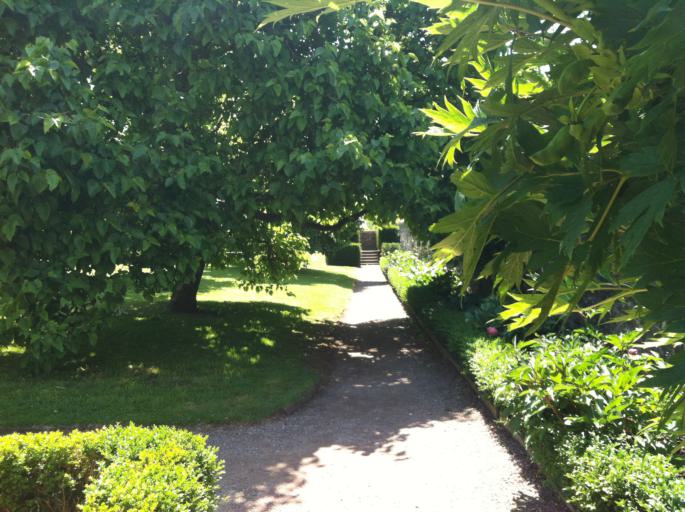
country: GB
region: Wales
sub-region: Cardiff
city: Radyr
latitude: 51.4873
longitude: -3.2694
